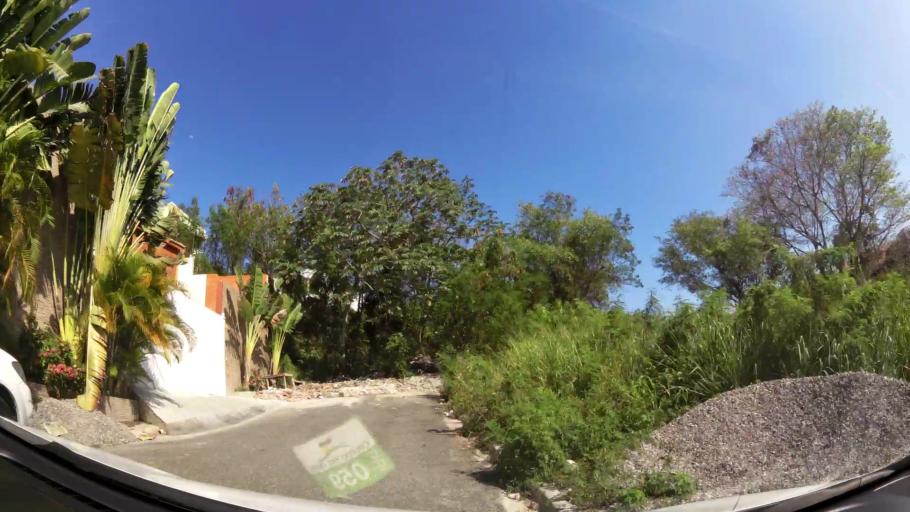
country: DO
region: Nacional
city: Bella Vista
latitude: 18.4603
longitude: -69.9829
